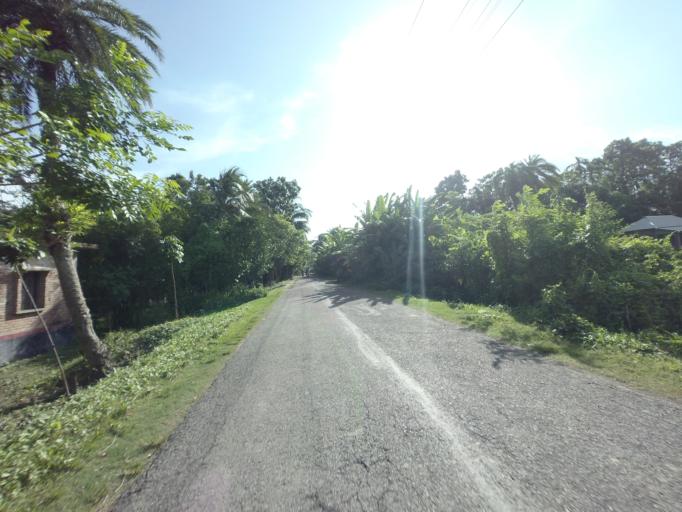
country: BD
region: Khulna
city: Kalia
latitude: 23.0132
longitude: 89.5906
